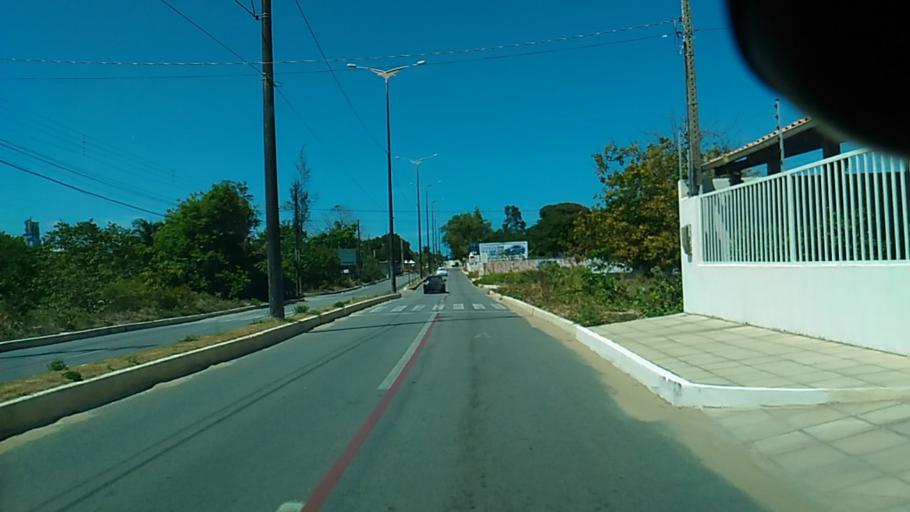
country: BR
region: Paraiba
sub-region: Joao Pessoa
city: Joao Pessoa
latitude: -7.1468
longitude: -34.8170
